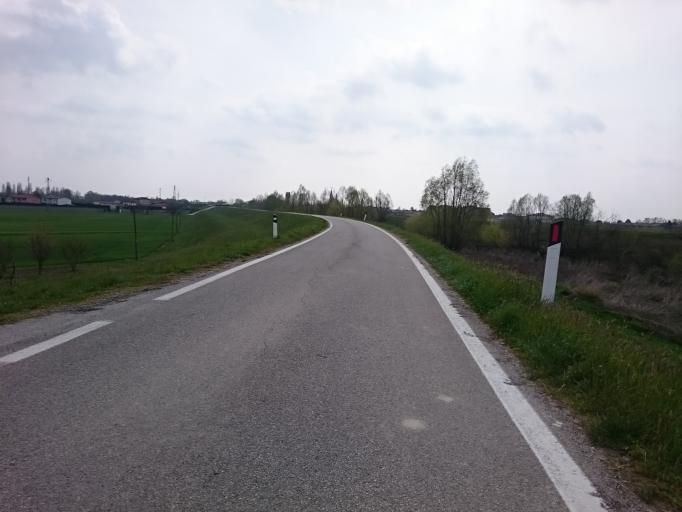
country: IT
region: Veneto
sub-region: Provincia di Padova
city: Bovolenta
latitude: 45.2765
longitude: 11.9342
